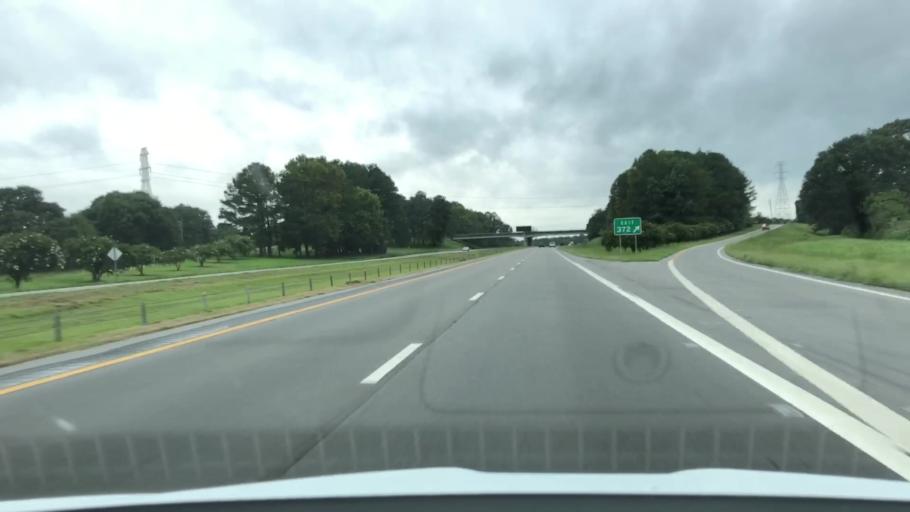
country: US
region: North Carolina
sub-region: Lenoir County
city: La Grange
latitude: 35.2892
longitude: -77.7828
